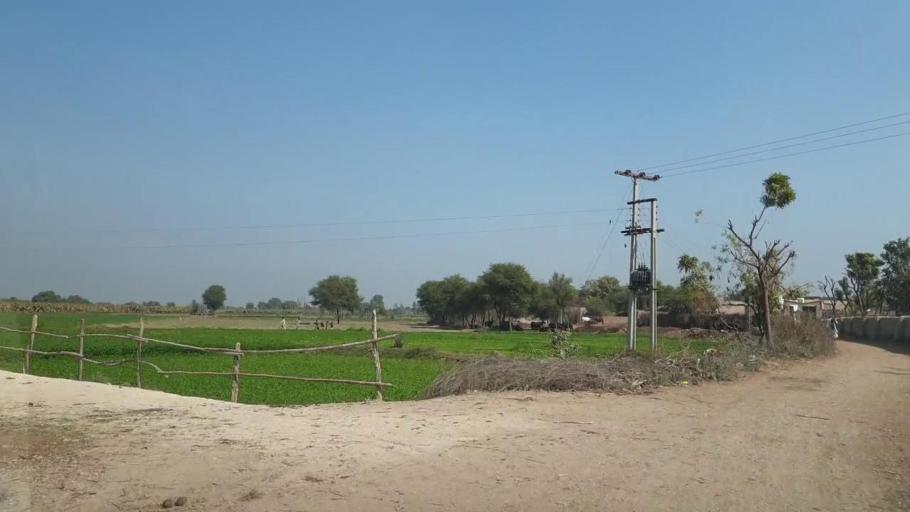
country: PK
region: Sindh
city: Tando Jam
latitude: 25.4970
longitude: 68.4762
